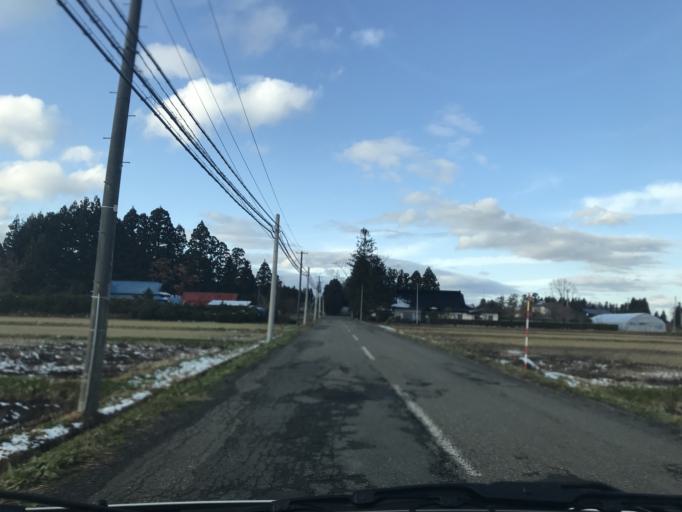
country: JP
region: Iwate
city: Kitakami
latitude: 39.2169
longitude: 141.0473
